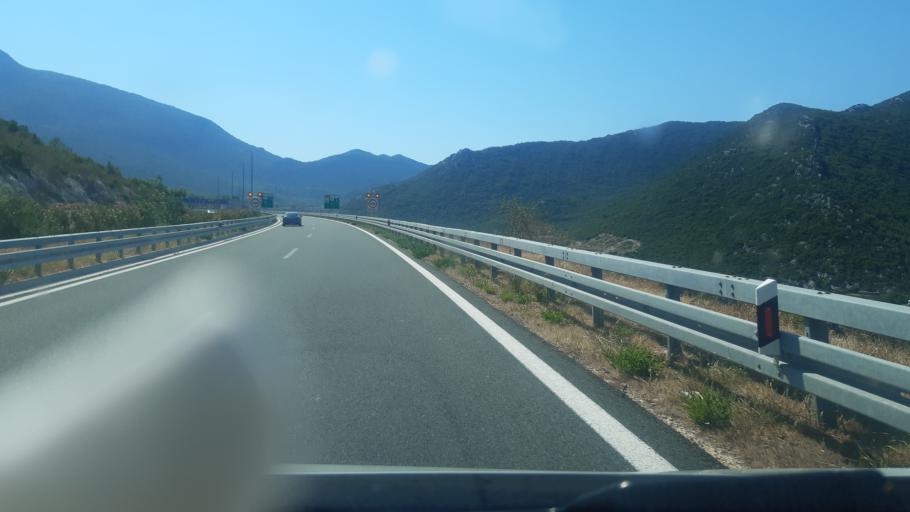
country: HR
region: Dubrovacko-Neretvanska
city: Komin
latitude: 43.1046
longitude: 17.4806
